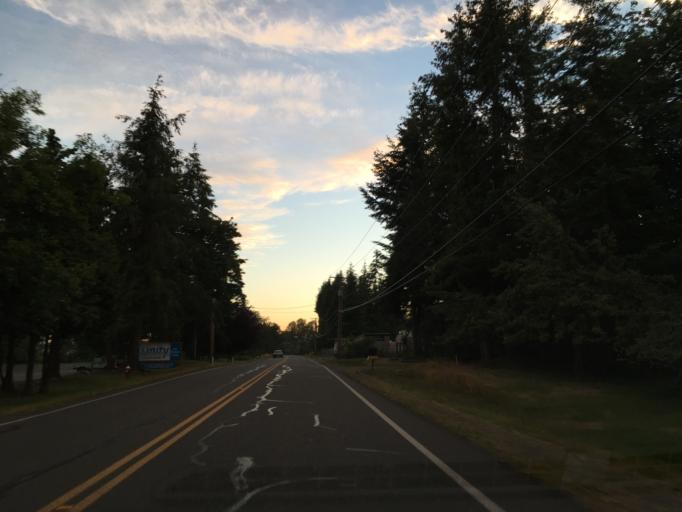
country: US
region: Washington
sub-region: Whatcom County
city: Bellingham
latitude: 48.7859
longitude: -122.4660
